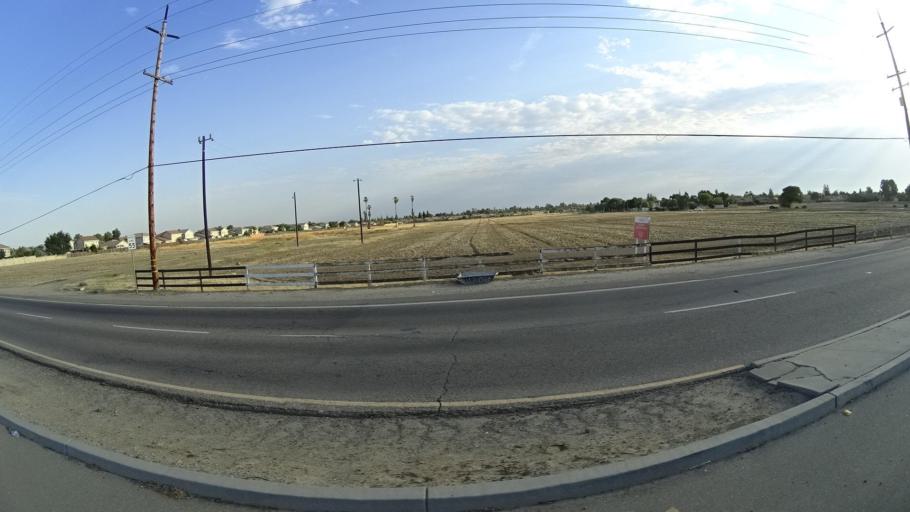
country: US
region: California
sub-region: Fresno County
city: Sunnyside
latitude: 36.7069
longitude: -119.7092
